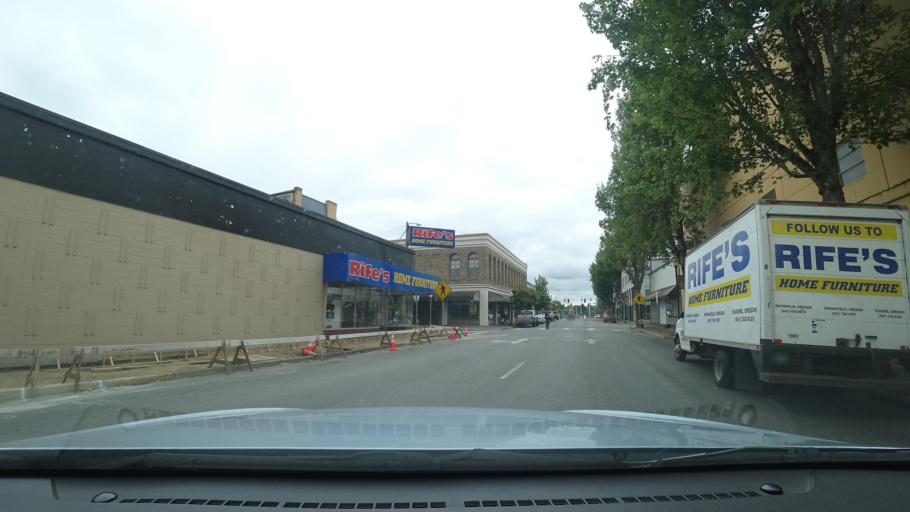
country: US
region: Oregon
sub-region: Coos County
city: Coos Bay
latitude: 43.3672
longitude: -124.2146
